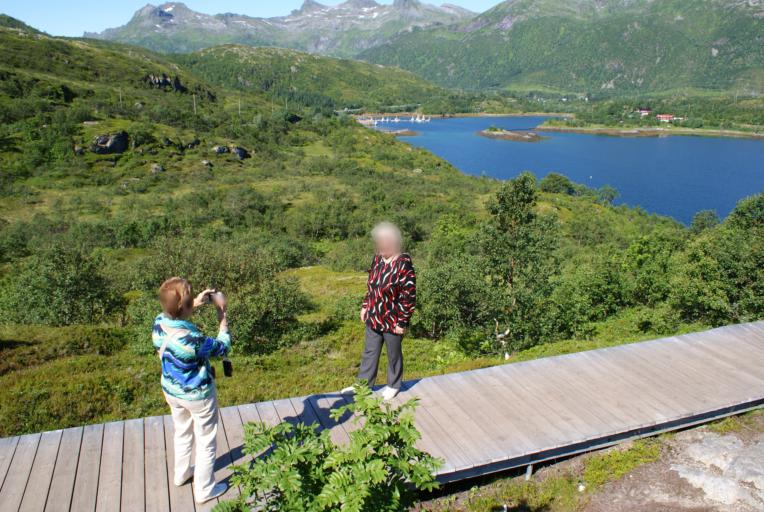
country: NO
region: Nordland
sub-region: Vagan
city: Svolvaer
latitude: 68.3166
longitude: 14.7169
